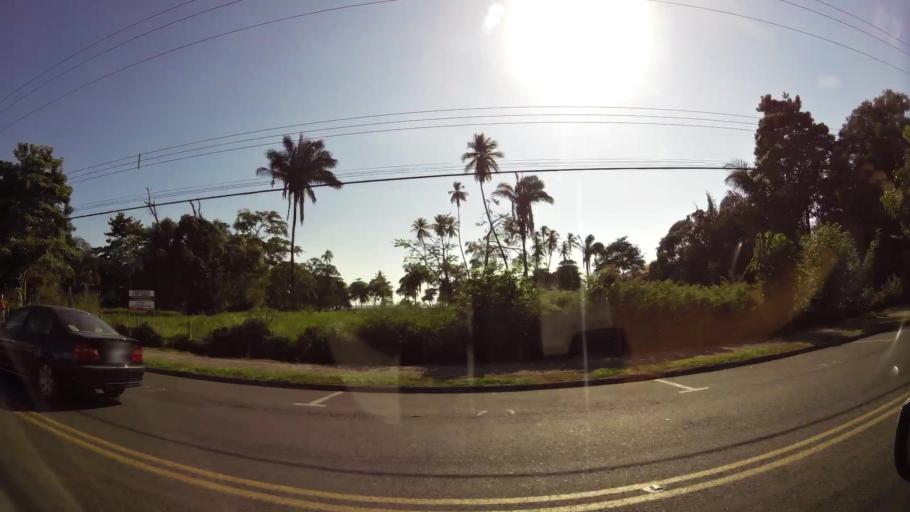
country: CR
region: Puntarenas
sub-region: Canton de Garabito
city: Jaco
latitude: 9.6198
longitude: -84.6343
